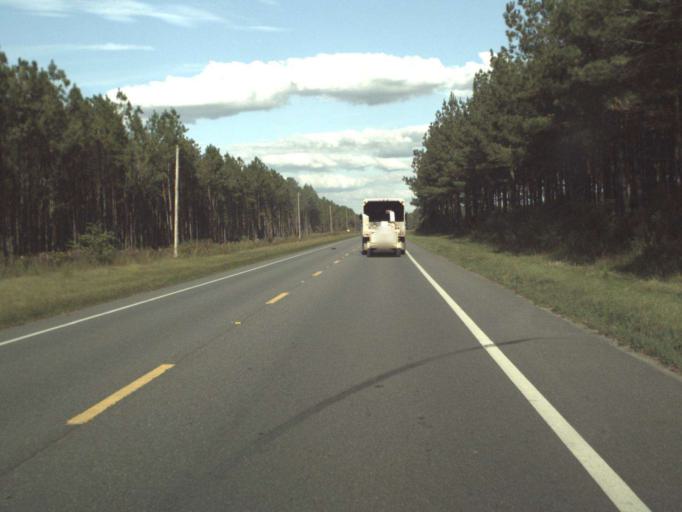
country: US
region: Florida
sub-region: Holmes County
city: Bonifay
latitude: 30.6518
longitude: -85.6726
